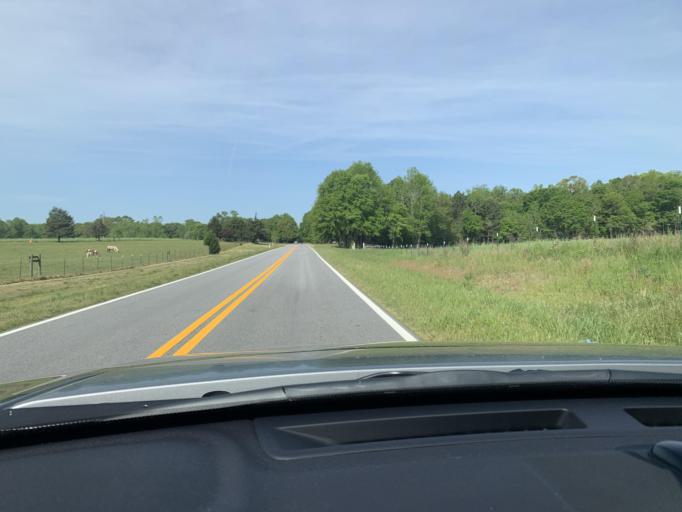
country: US
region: Georgia
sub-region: Oconee County
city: Watkinsville
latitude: 33.8136
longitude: -83.4100
